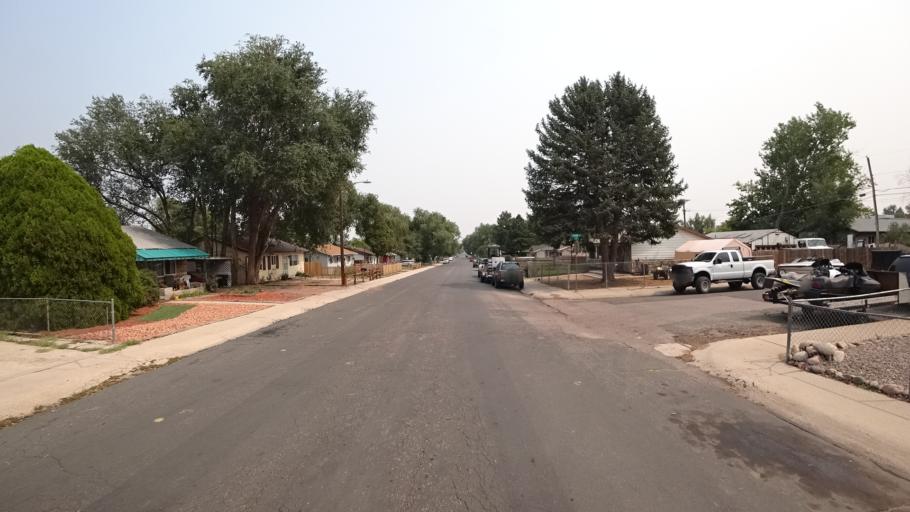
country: US
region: Colorado
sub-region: El Paso County
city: Colorado Springs
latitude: 38.7988
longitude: -104.8129
